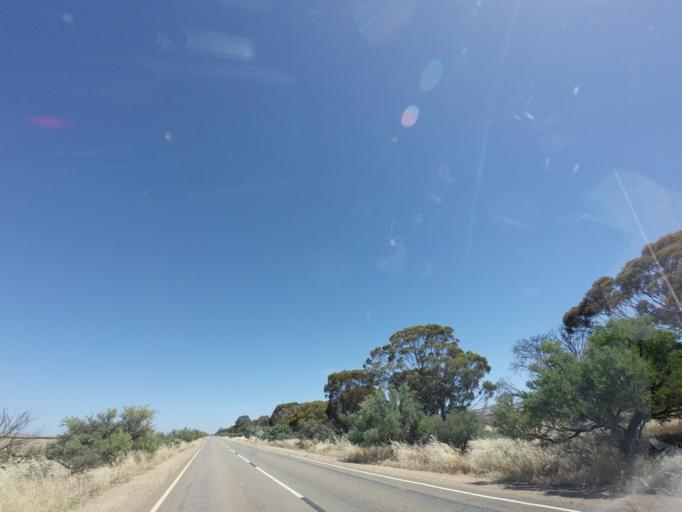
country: AU
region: South Australia
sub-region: Peterborough
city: Peterborough
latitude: -32.7768
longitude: 138.6646
